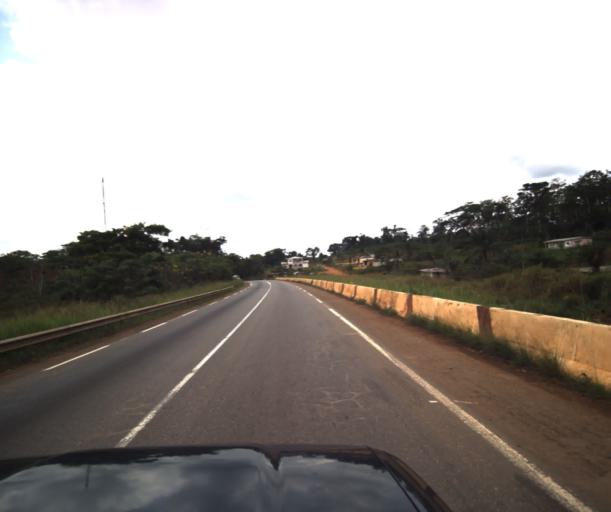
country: CM
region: Centre
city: Eseka
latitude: 3.8526
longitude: 10.9678
